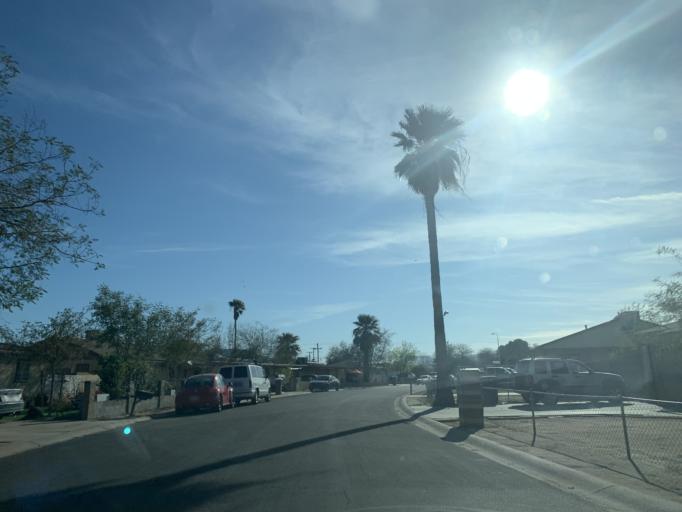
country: US
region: Arizona
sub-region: Maricopa County
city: Laveen
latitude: 33.4044
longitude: -112.1369
